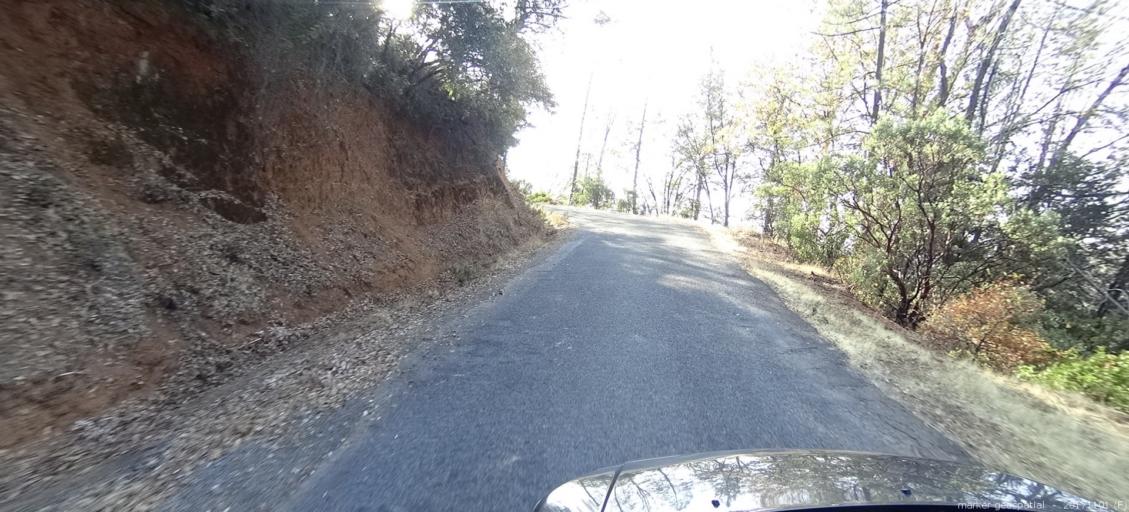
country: US
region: California
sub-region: Shasta County
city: Shasta Lake
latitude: 40.8101
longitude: -122.3147
